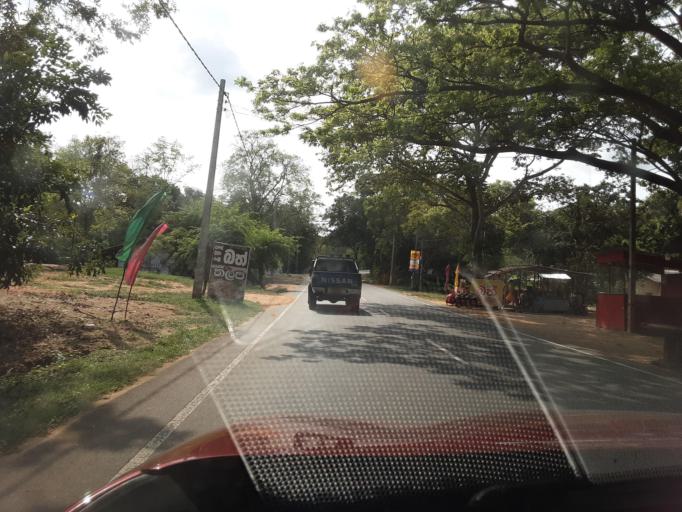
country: LK
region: Uva
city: Haputale
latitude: 6.3565
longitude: 81.1886
